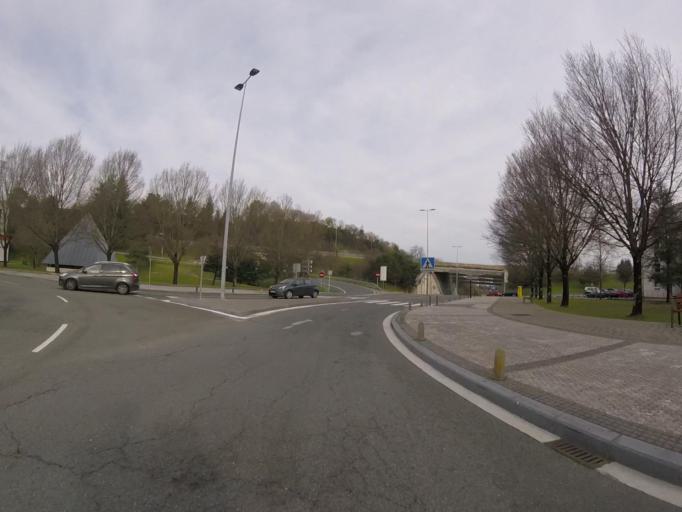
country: ES
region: Basque Country
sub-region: Provincia de Guipuzcoa
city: Lasarte
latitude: 43.2980
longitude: -2.0071
